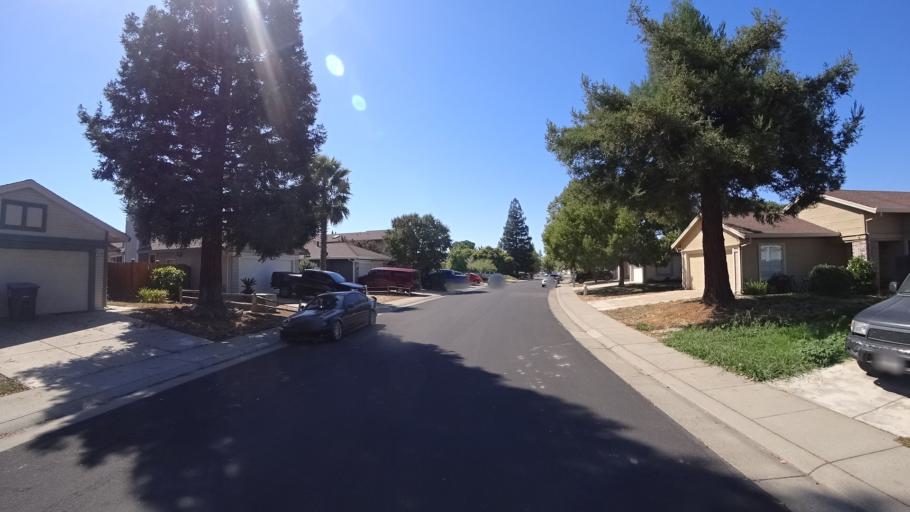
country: US
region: California
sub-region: Sacramento County
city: Laguna
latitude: 38.4334
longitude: -121.4394
